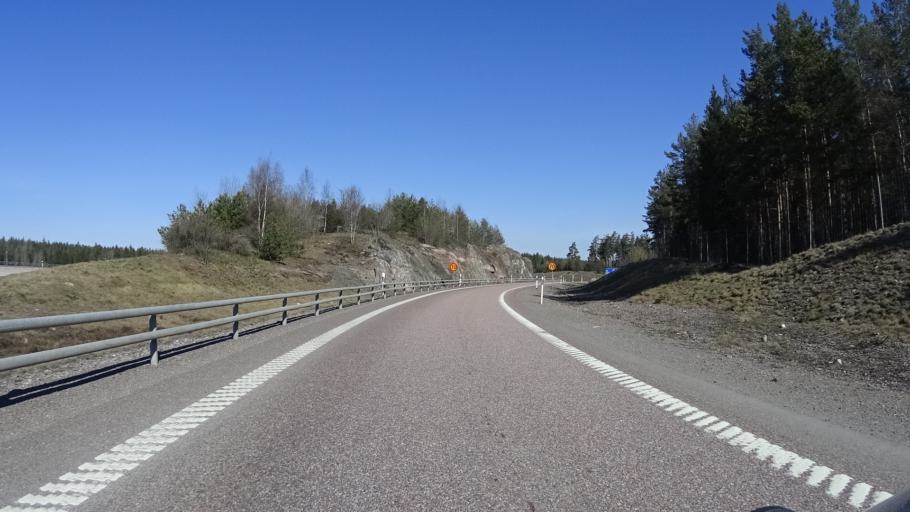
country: SE
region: Soedermanland
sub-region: Strangnas Kommun
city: Strangnas
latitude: 59.3290
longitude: 17.0204
